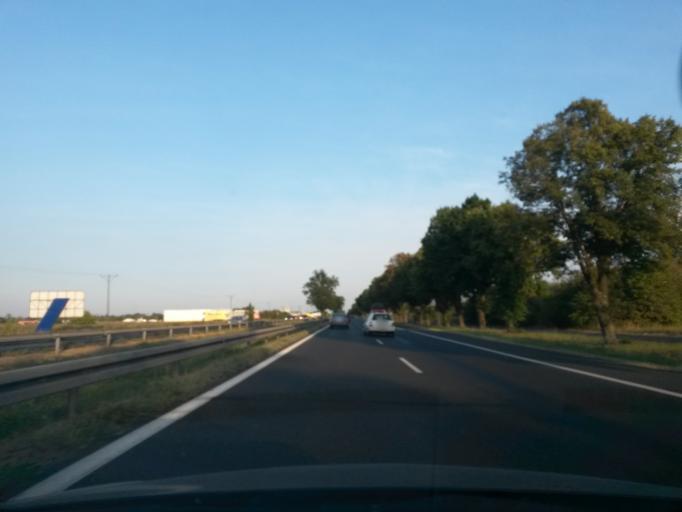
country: PL
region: Masovian Voivodeship
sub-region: Powiat nowodworski
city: Nowy Dwor Mazowiecki
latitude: 52.3834
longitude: 20.7545
